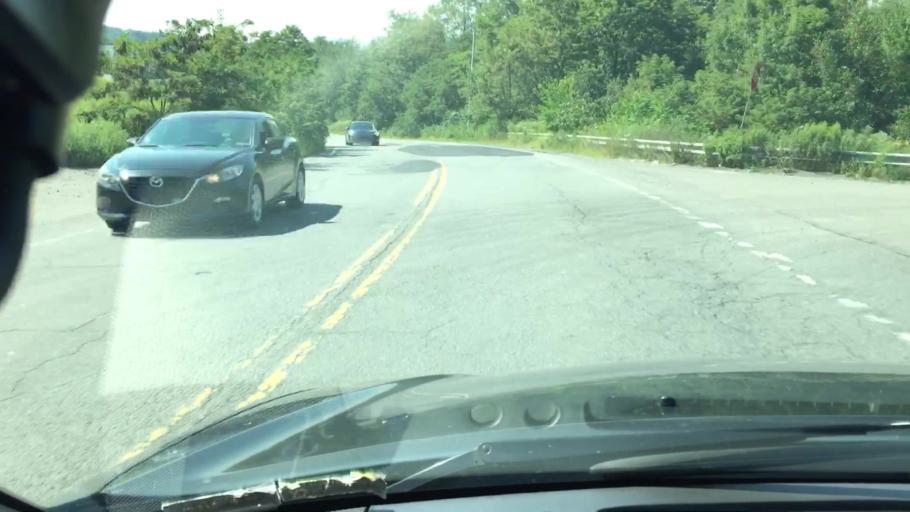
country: US
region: Pennsylvania
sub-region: Luzerne County
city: Ashley
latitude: 41.2015
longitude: -75.9199
